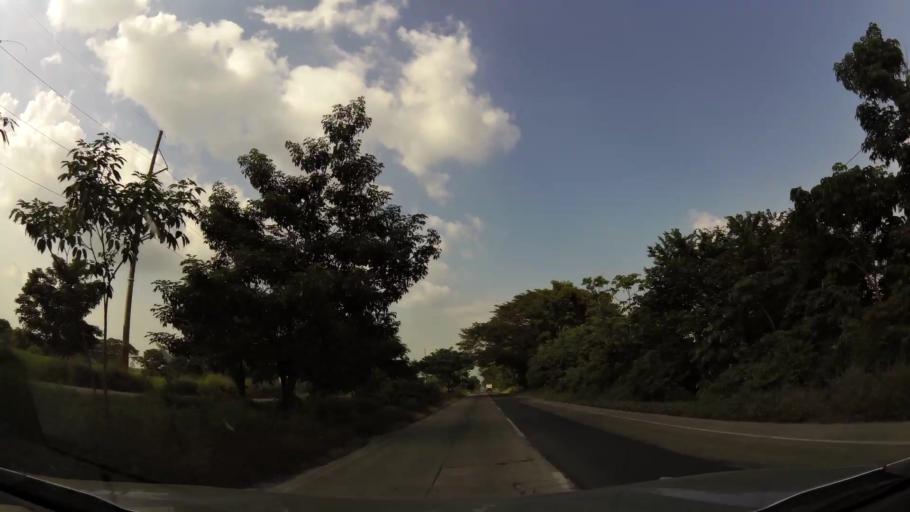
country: GT
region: Escuintla
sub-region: Municipio de Masagua
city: Masagua
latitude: 14.0815
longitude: -90.7781
